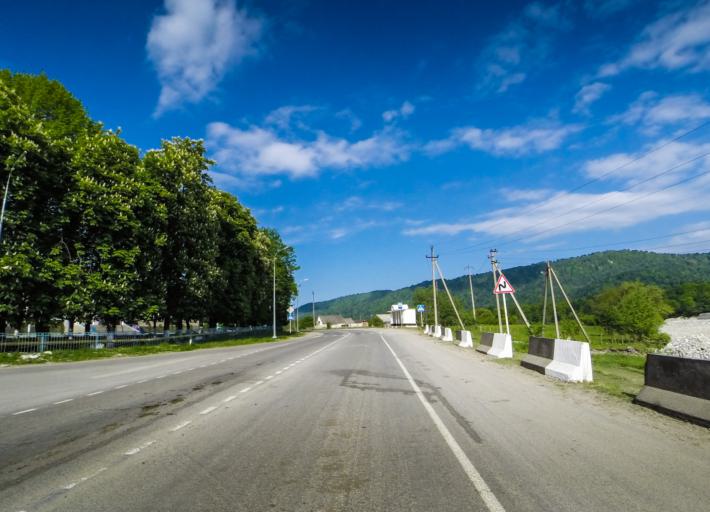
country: RU
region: Kabardino-Balkariya
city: Babugent
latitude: 43.2832
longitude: 43.5549
